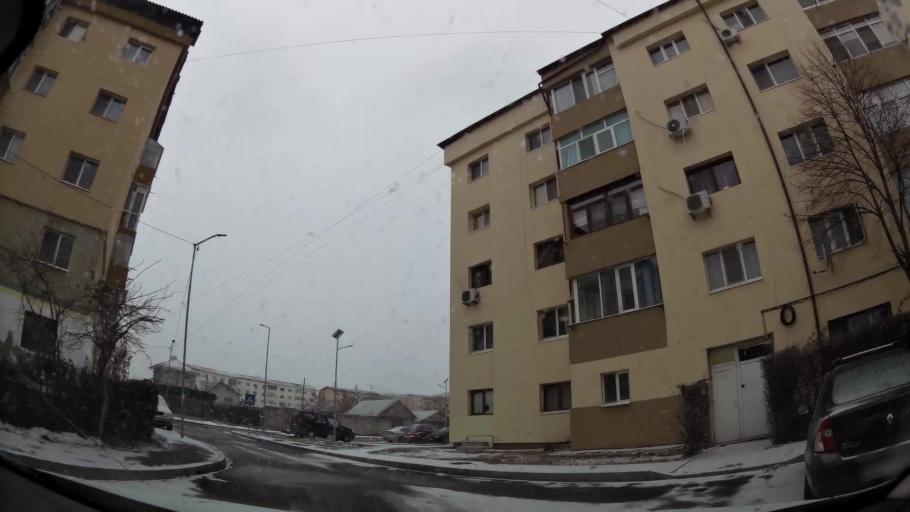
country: RO
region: Dambovita
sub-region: Municipiul Targoviste
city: Targoviste
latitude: 44.9144
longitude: 25.4758
